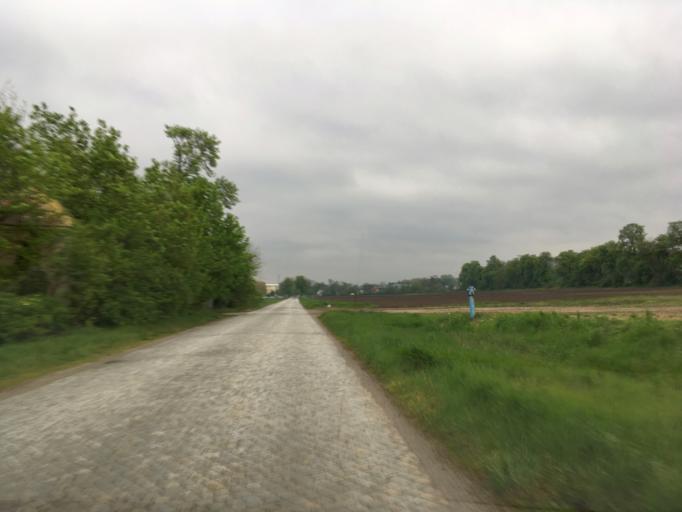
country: AT
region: Lower Austria
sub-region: Politischer Bezirk Bruck an der Leitha
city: Bruck an der Leitha
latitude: 48.0114
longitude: 16.7670
